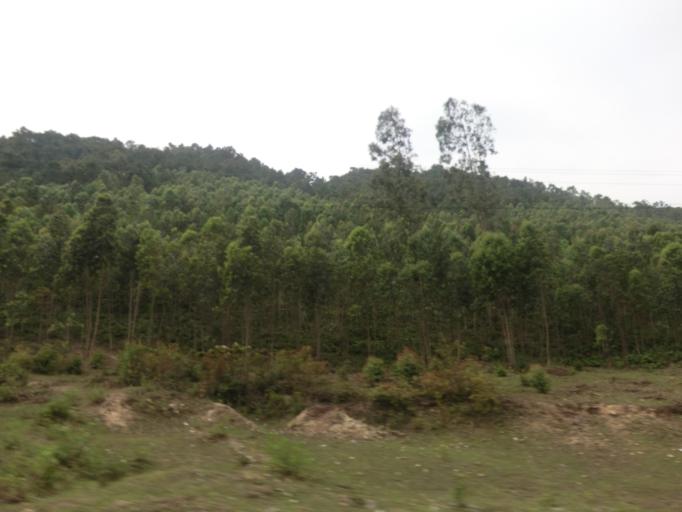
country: VN
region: Nghe An
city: Cau Giat
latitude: 19.1783
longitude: 105.5986
